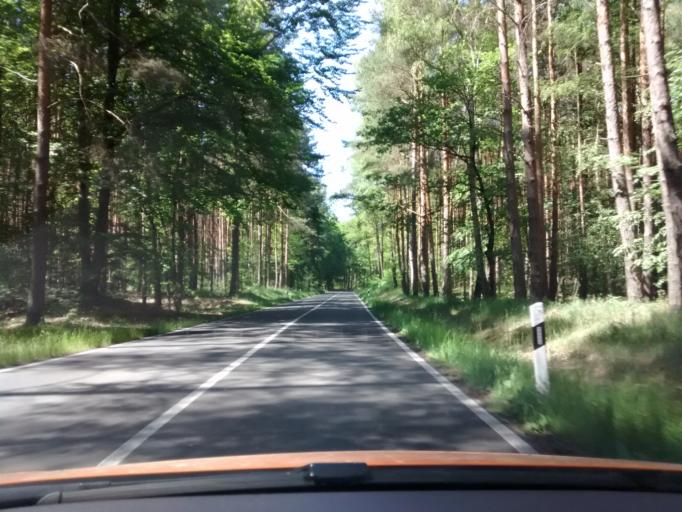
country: DE
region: Brandenburg
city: Wendisch Rietz
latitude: 52.2287
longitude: 13.9976
